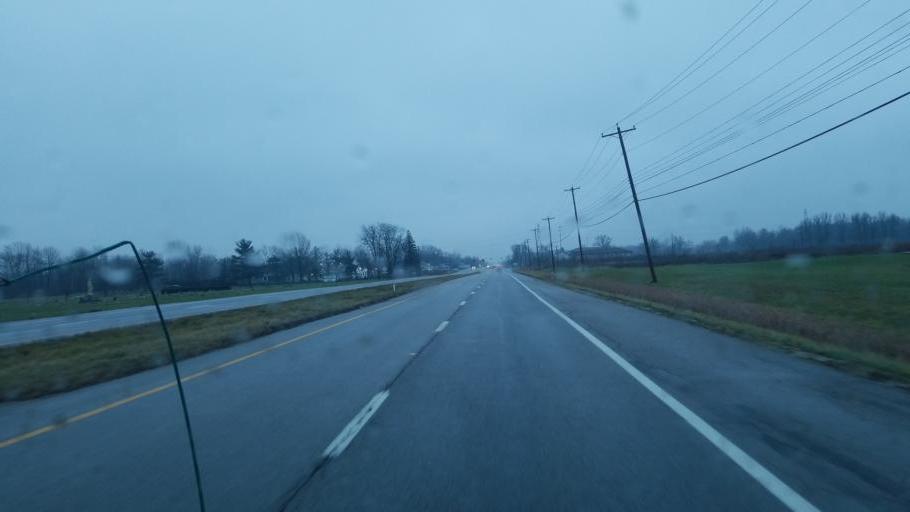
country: US
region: Ohio
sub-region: Delaware County
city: Lewis Center
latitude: 40.2254
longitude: -83.0364
